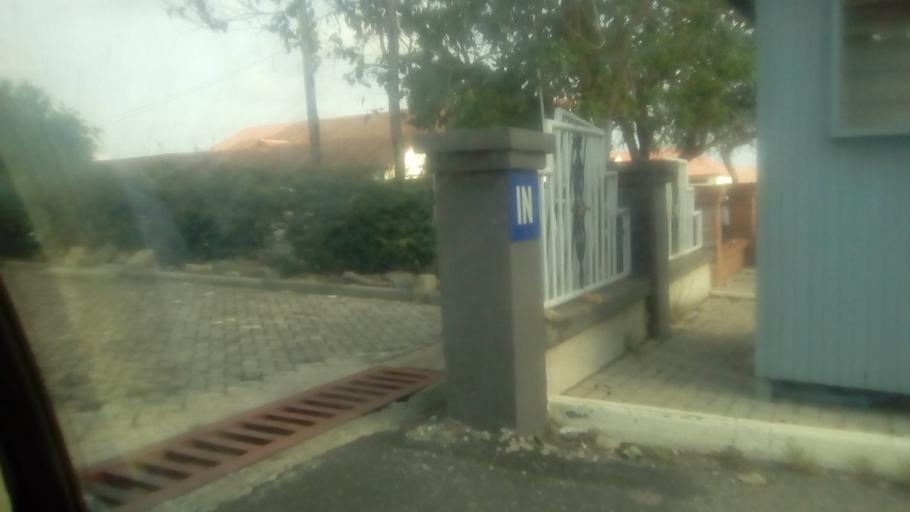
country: GH
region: Greater Accra
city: Medina Estates
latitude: 5.6549
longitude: -0.1899
